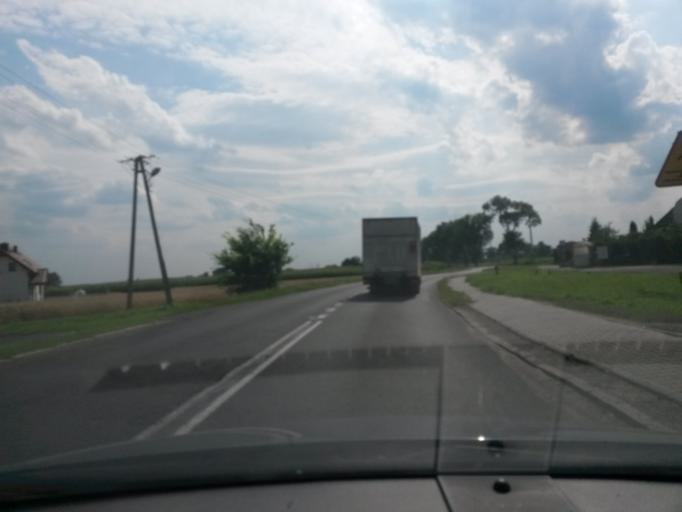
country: PL
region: Greater Poland Voivodeship
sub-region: Powiat poznanski
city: Kleszczewo
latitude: 52.3038
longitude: 17.1294
